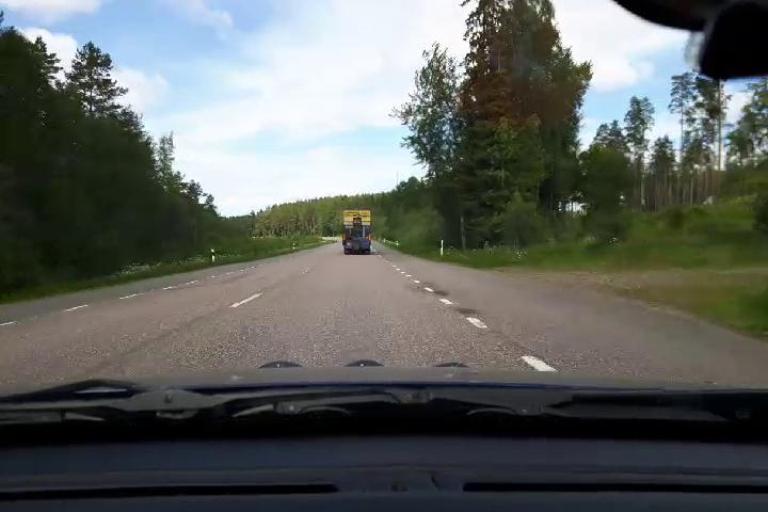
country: SE
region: Uppsala
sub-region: Osthammars Kommun
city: Bjorklinge
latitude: 60.0976
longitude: 17.5537
